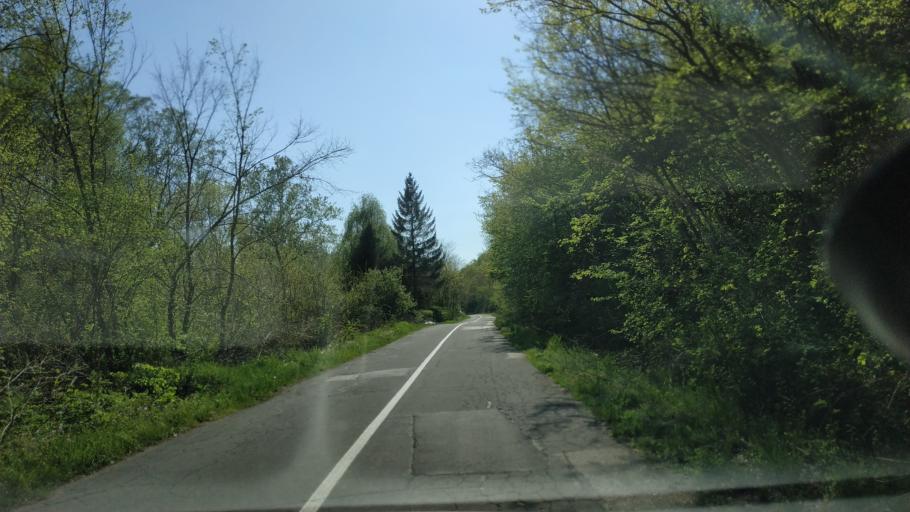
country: RS
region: Central Serbia
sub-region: Nisavski Okrug
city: Nis
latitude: 43.4177
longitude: 21.8411
